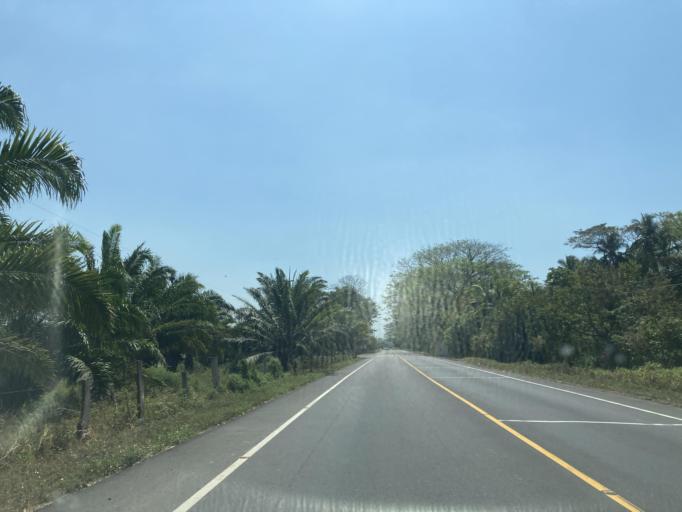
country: GT
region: Escuintla
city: Guanagazapa
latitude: 14.1148
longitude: -90.6357
